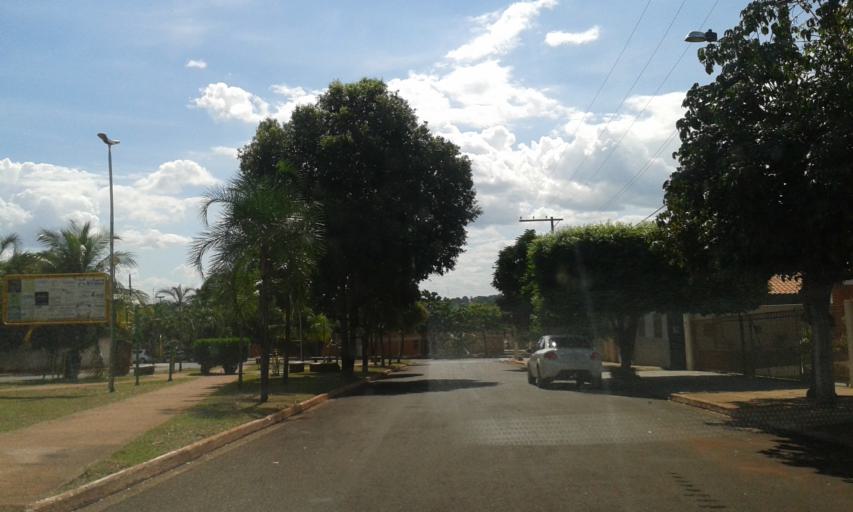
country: BR
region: Minas Gerais
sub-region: Santa Vitoria
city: Santa Vitoria
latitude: -18.8397
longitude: -50.1218
